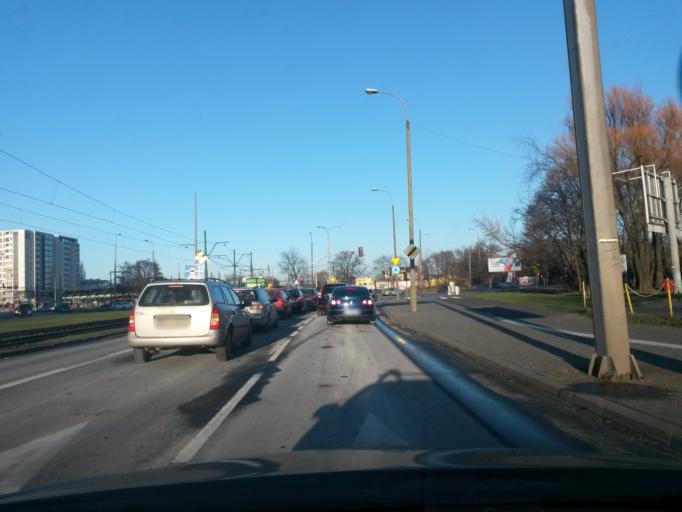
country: PL
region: Greater Poland Voivodeship
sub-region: Poznan
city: Poznan
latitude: 52.3944
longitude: 16.9498
